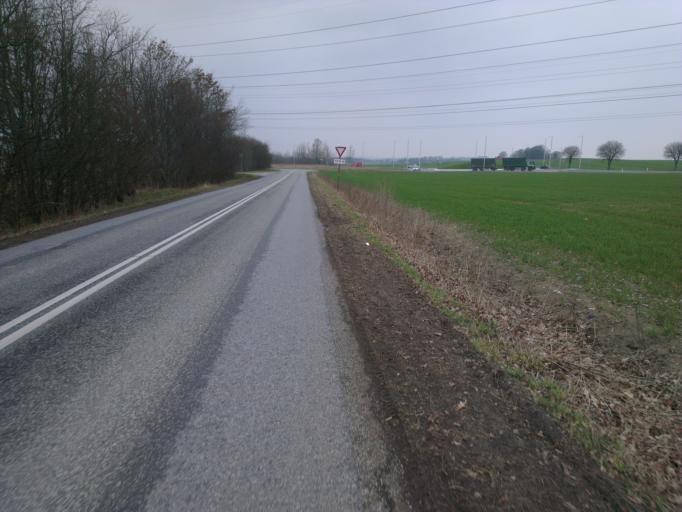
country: DK
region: Capital Region
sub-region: Frederikssund Kommune
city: Slangerup
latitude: 55.8508
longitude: 12.1578
